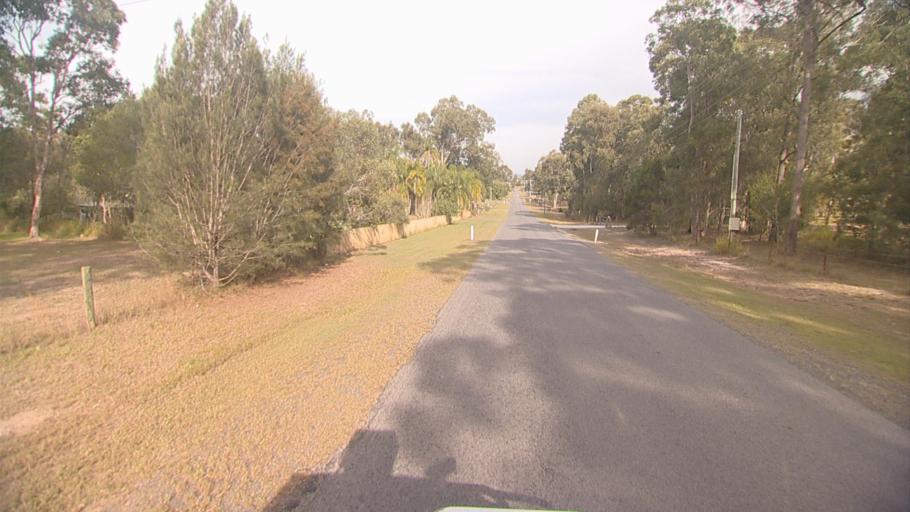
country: AU
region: Queensland
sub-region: Logan
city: Chambers Flat
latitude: -27.7984
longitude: 153.1226
